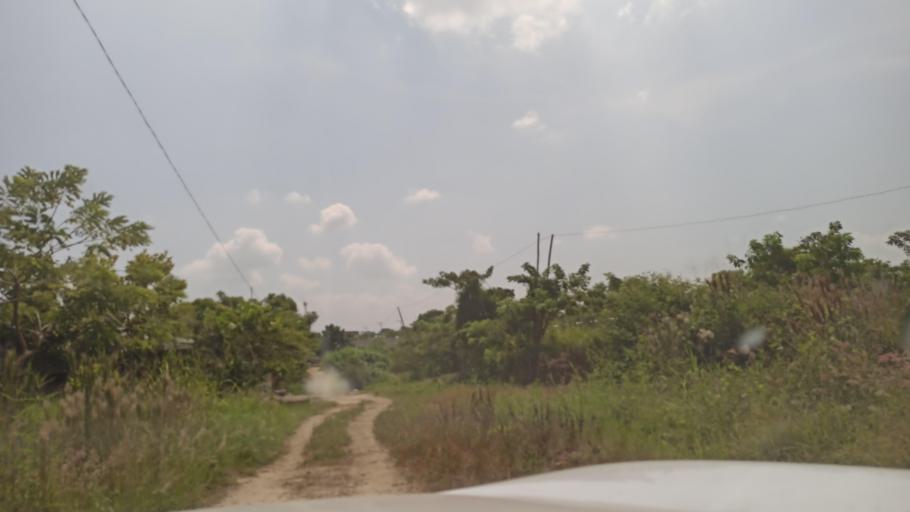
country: MX
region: Veracruz
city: Martinez de la Torre
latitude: 20.0801
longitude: -97.0768
